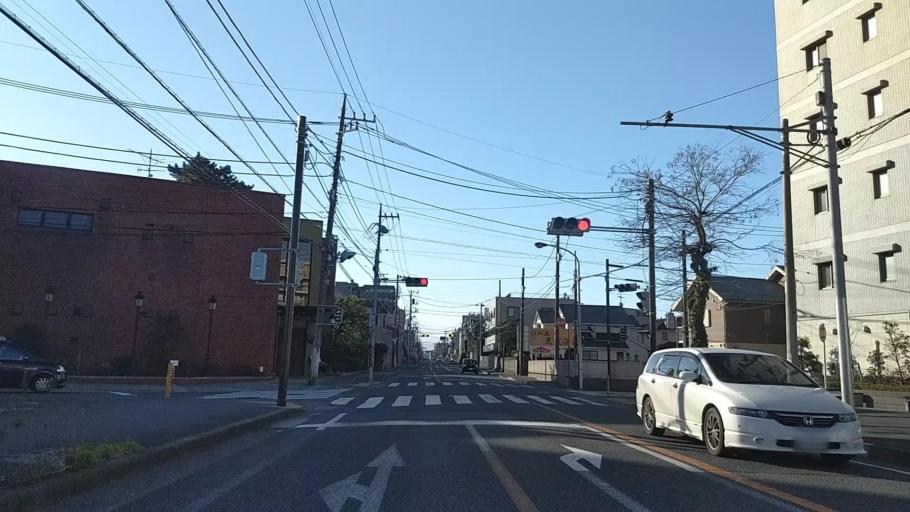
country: JP
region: Kanagawa
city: Fujisawa
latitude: 35.3286
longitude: 139.4875
